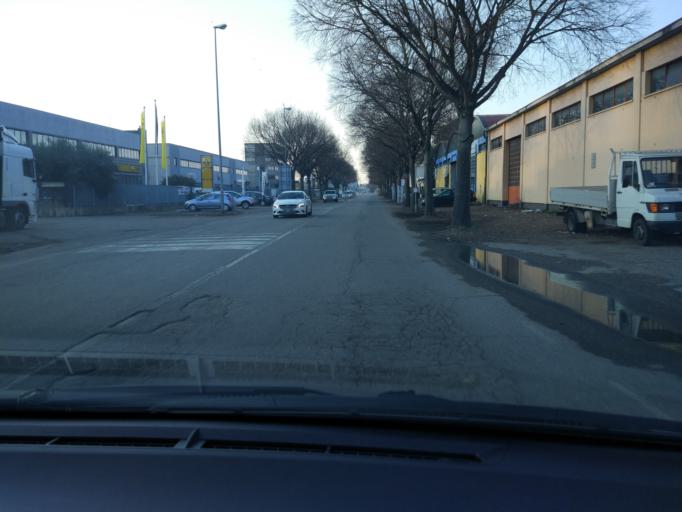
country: IT
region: Veneto
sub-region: Provincia di Verona
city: Verona
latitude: 45.4057
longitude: 10.9674
